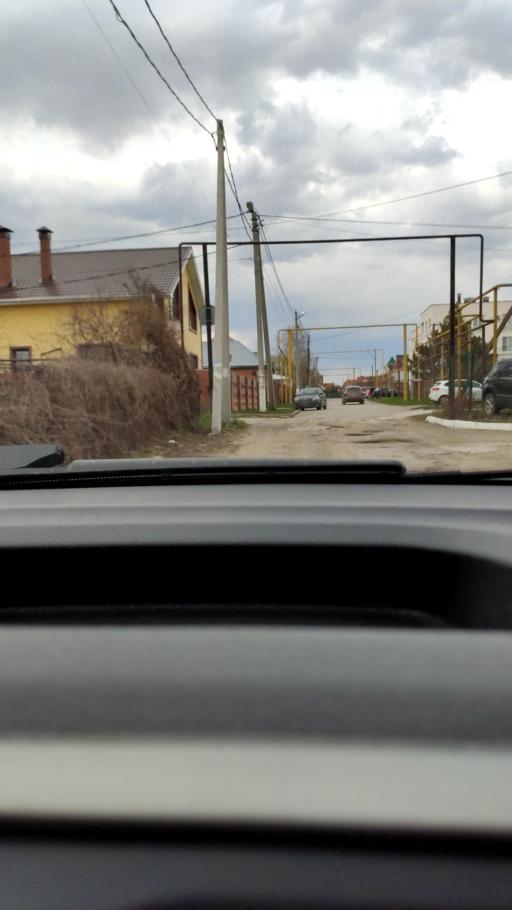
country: RU
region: Samara
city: Podstepki
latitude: 53.5085
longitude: 49.2373
